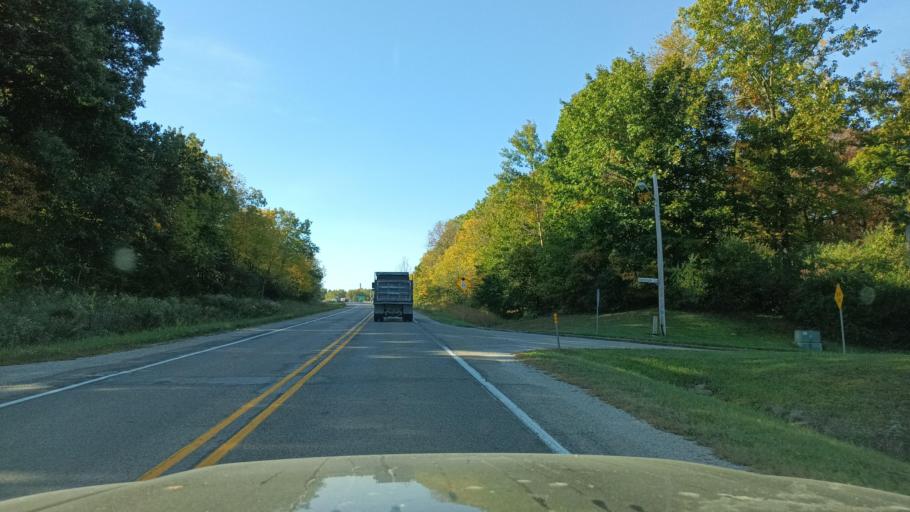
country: US
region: Illinois
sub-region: Clark County
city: Marshall
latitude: 39.4292
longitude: -87.6913
